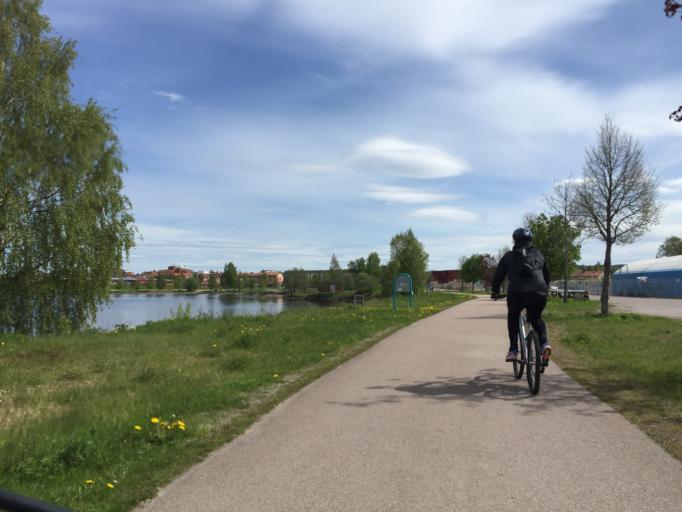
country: SE
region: Dalarna
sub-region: Ludvika Kommun
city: Ludvika
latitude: 60.1484
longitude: 15.1716
